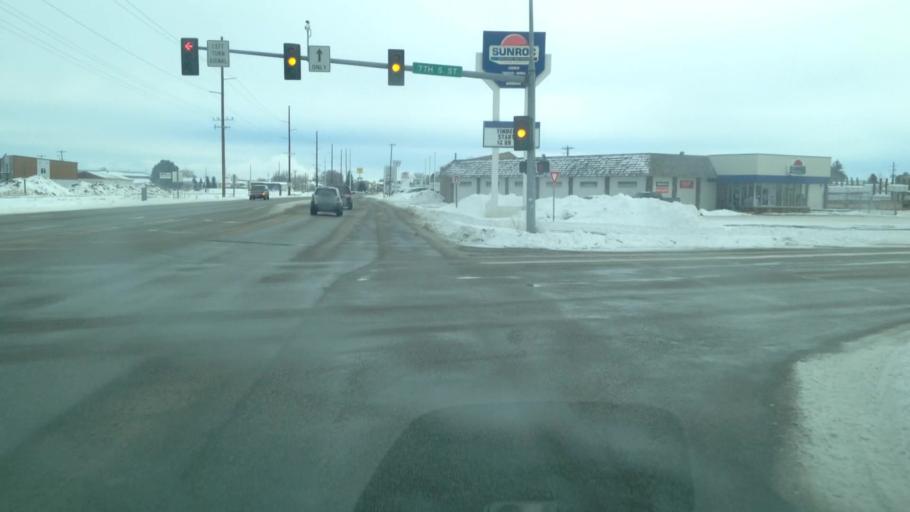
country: US
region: Idaho
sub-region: Madison County
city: Rexburg
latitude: 43.8116
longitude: -111.8024
